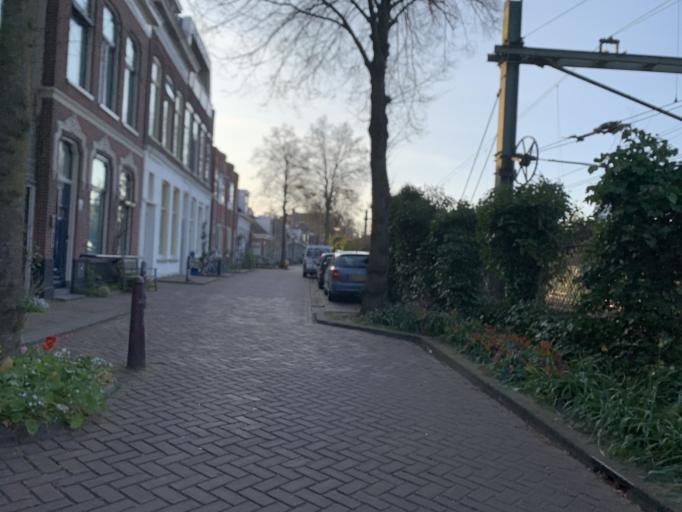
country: NL
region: Groningen
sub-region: Gemeente Groningen
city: Groningen
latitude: 53.2105
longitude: 6.5733
